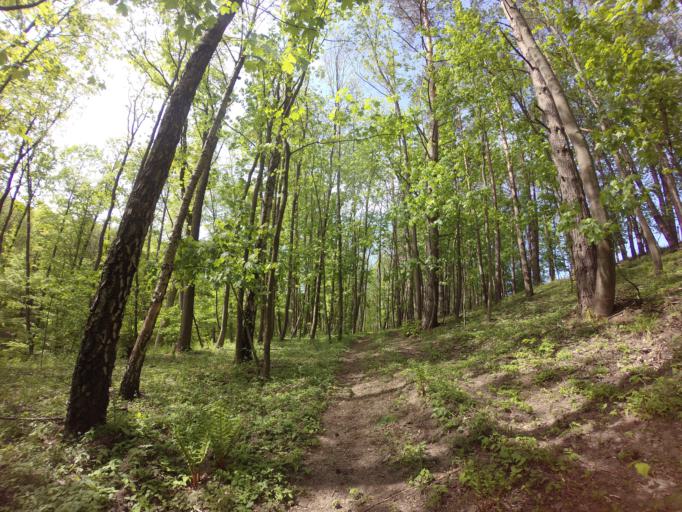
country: PL
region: West Pomeranian Voivodeship
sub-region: Powiat choszczenski
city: Choszczno
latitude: 53.2249
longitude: 15.4180
